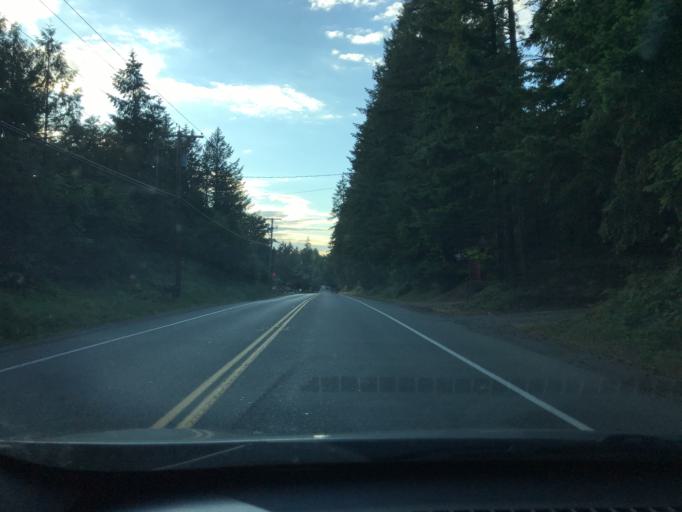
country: US
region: Washington
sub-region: King County
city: Lake Morton-Berrydale
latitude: 47.3111
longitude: -122.0933
